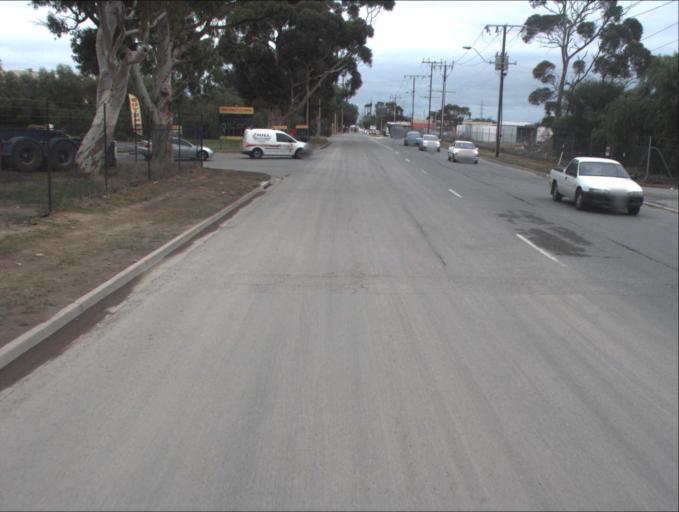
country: AU
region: South Australia
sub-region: Port Adelaide Enfield
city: Enfield
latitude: -34.8318
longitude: 138.5940
